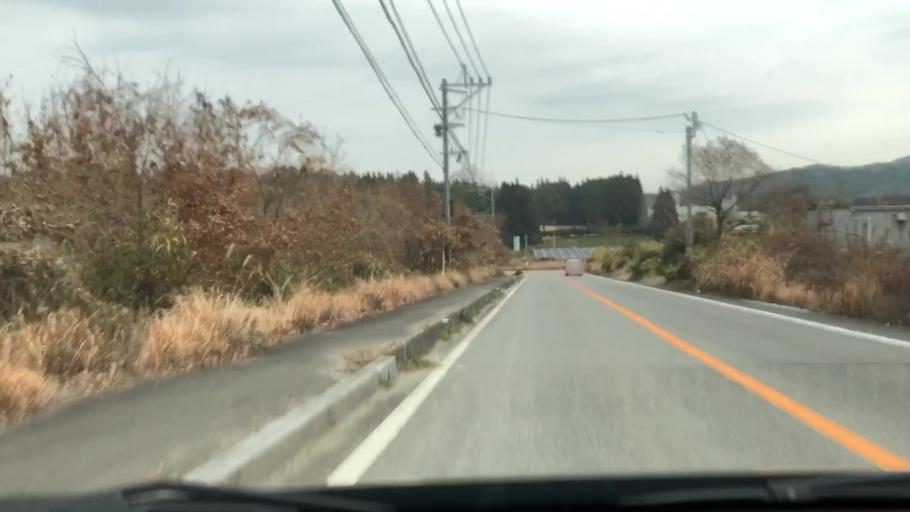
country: JP
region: Oita
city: Usuki
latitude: 33.0065
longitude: 131.6306
